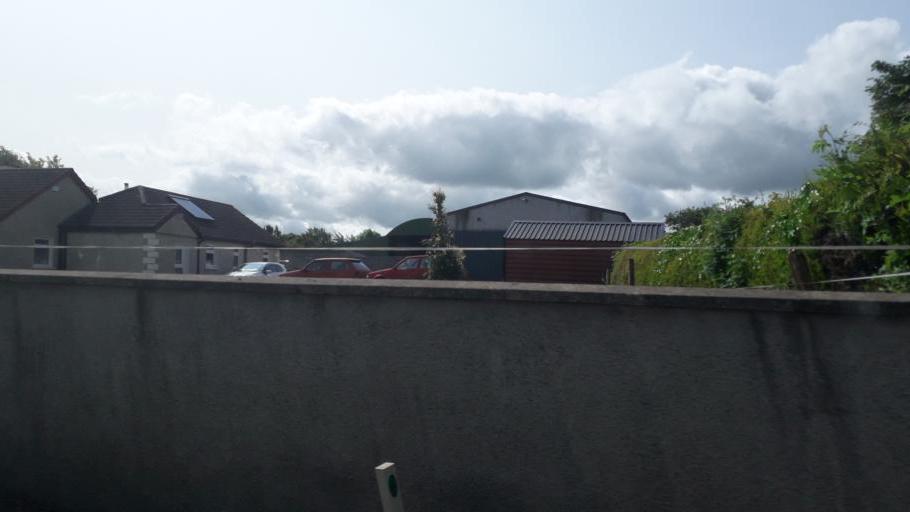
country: IE
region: Leinster
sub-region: Kilkenny
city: Graiguenamanagh
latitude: 52.6059
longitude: -7.0120
